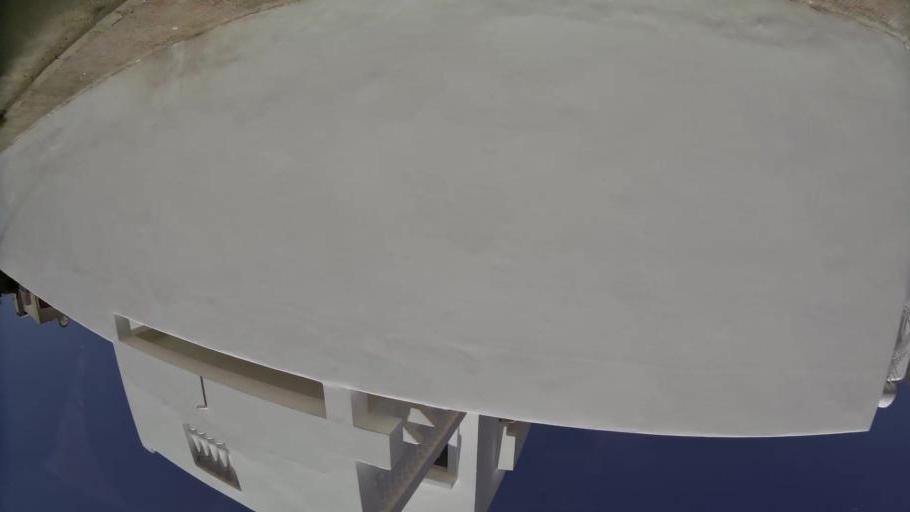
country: MA
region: Souss-Massa-Draa
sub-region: Agadir-Ida-ou-Tnan
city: Agadir
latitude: 30.4360
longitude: -9.5842
